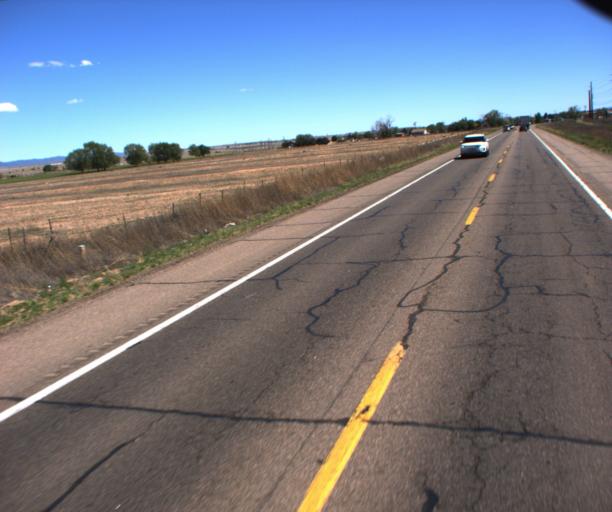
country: US
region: Arizona
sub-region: Yavapai County
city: Chino Valley
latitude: 34.8086
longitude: -112.4514
